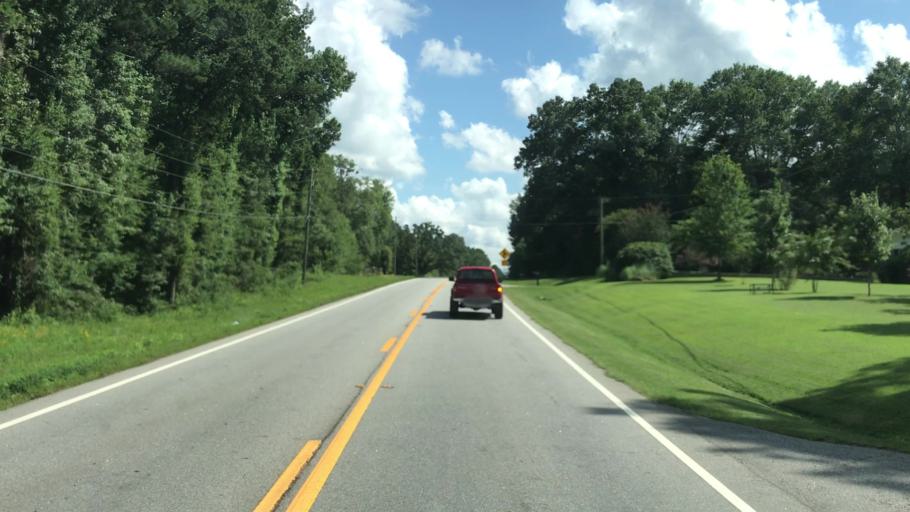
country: US
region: Georgia
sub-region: Walton County
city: Walnut Grove
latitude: 33.6861
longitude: -83.8505
